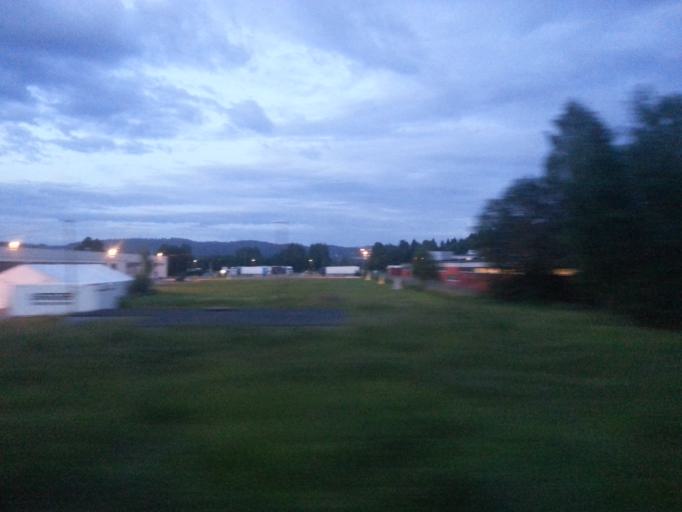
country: NO
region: Akershus
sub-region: Skedsmo
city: Lillestrom
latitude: 59.9648
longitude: 11.0666
